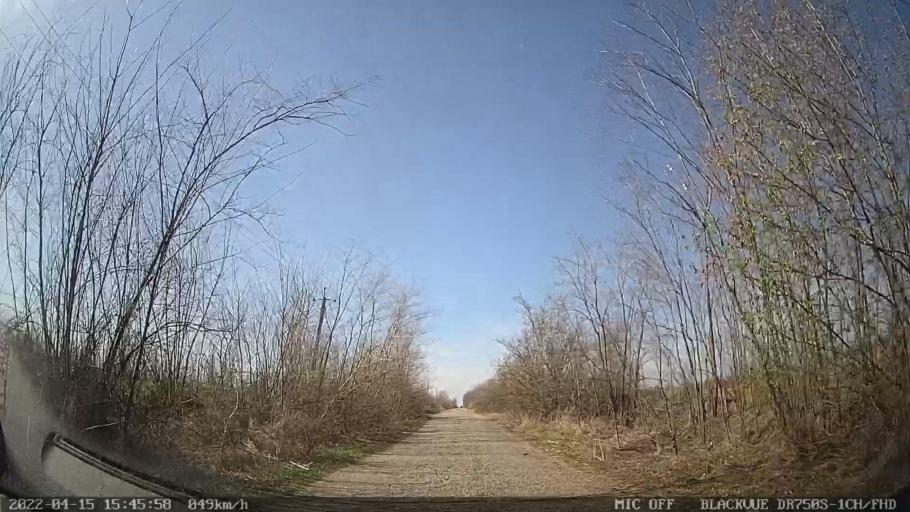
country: MD
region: Raionul Ocnita
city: Otaci
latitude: 48.3792
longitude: 27.9158
